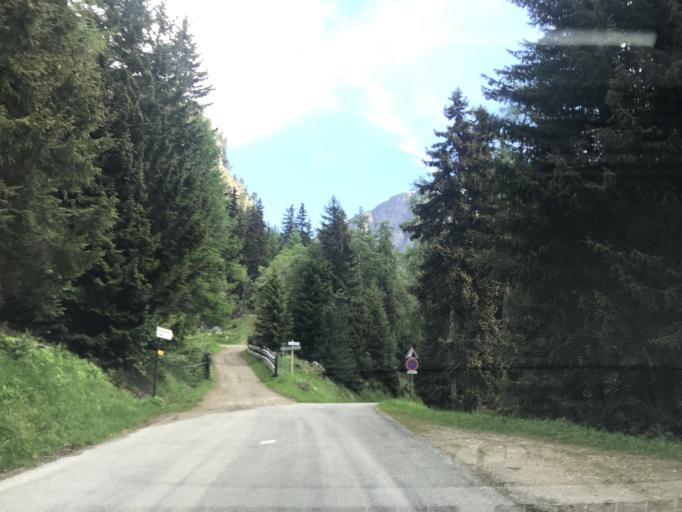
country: FR
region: Rhone-Alpes
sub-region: Departement de la Savoie
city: Modane
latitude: 45.2196
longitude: 6.6494
